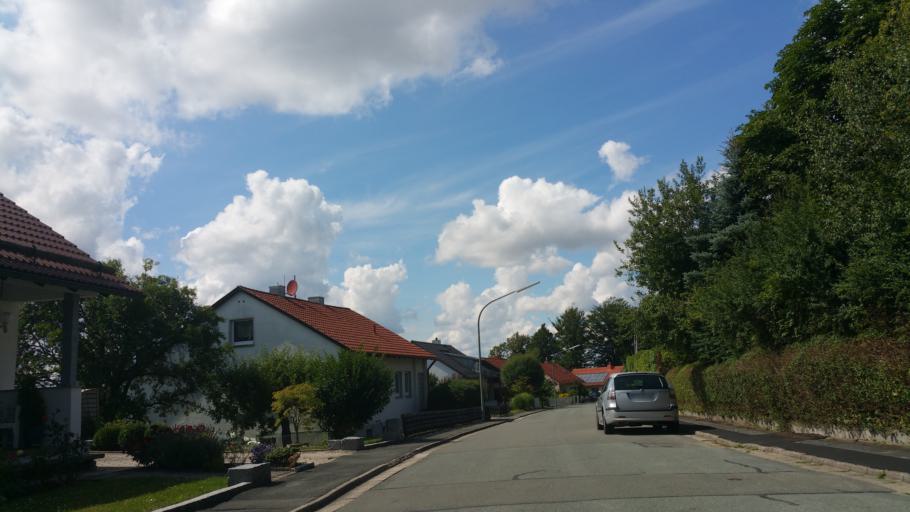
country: DE
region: Bavaria
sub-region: Upper Franconia
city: Oberkotzau
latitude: 50.2593
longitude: 11.9387
